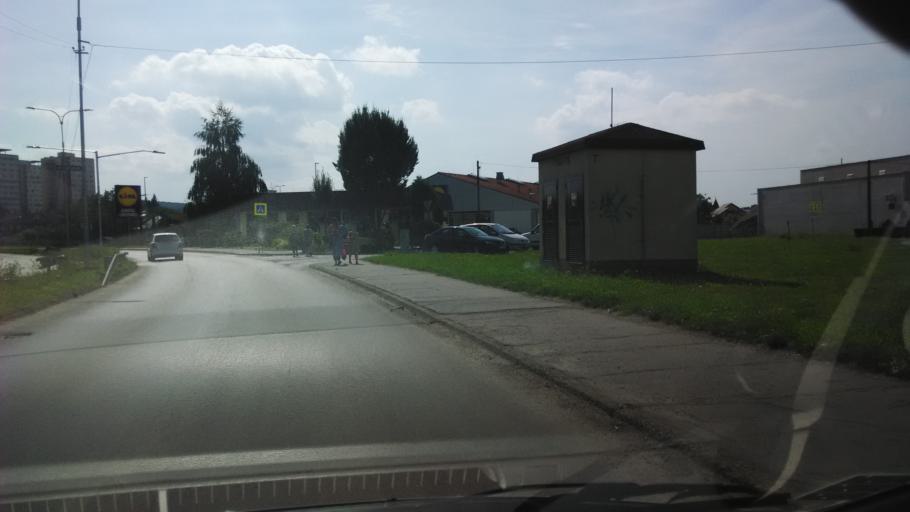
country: SK
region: Nitriansky
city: Banovce nad Bebravou
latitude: 48.7274
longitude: 18.2514
